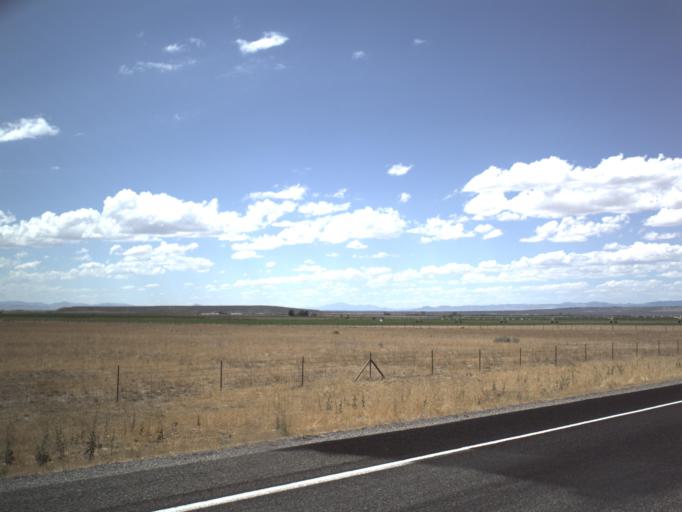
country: US
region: Utah
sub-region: Millard County
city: Fillmore
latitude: 39.1181
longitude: -112.3254
